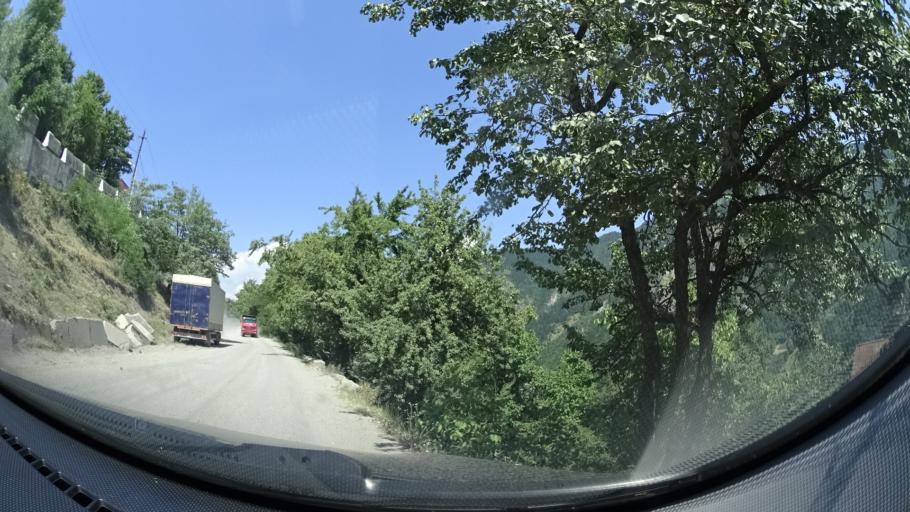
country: GE
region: Ajaria
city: Khulo
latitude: 41.6423
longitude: 42.3145
